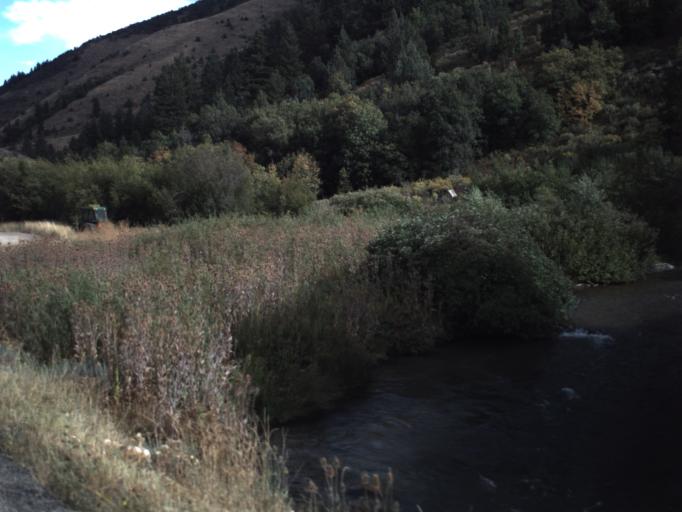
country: US
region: Utah
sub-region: Cache County
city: Millville
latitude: 41.6093
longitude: -111.6239
